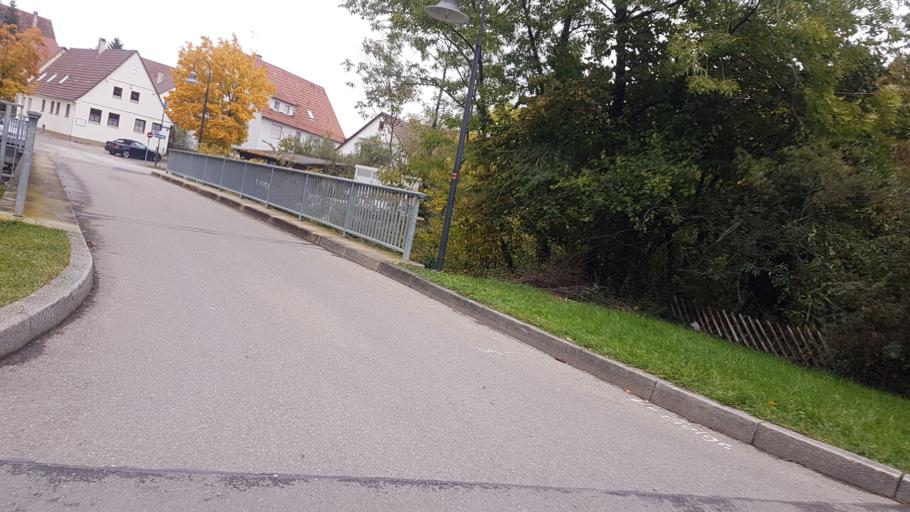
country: DE
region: Baden-Wuerttemberg
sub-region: Tuebingen Region
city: Dusslingen
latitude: 48.4473
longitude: 9.0553
